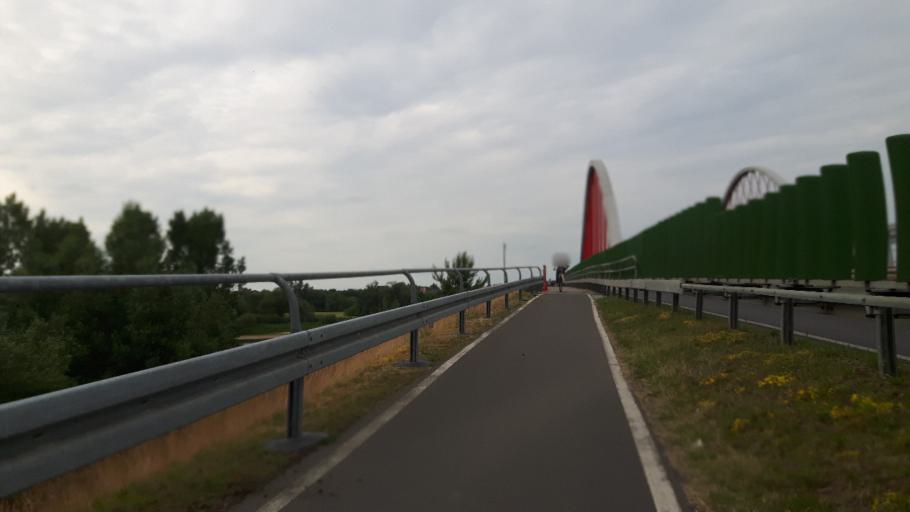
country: DE
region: Saxony-Anhalt
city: Wittenburg
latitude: 51.8557
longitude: 12.6508
